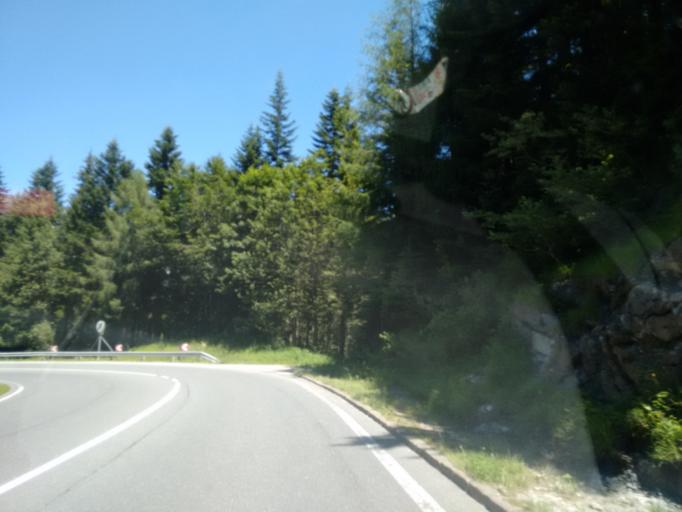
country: AT
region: Styria
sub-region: Politischer Bezirk Liezen
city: Altaussee
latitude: 47.6292
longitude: 13.6918
